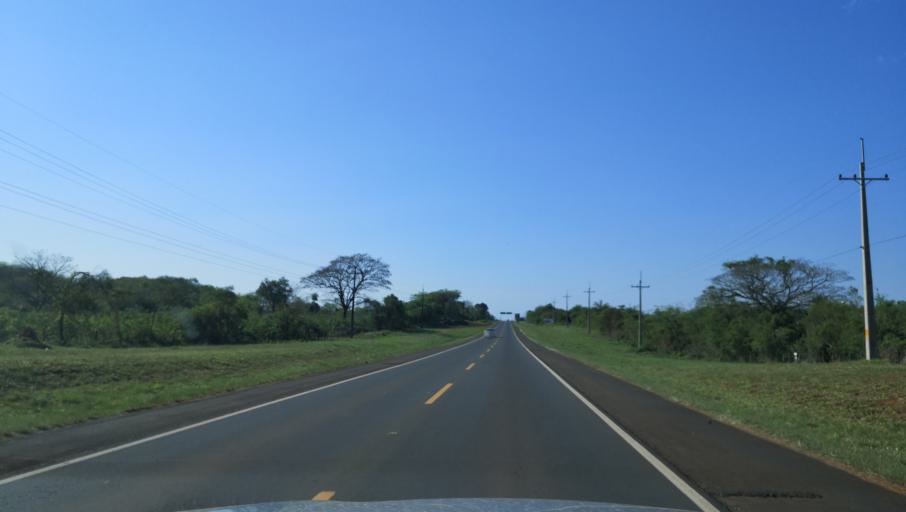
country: PY
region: Misiones
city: Santa Rosa
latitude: -26.9109
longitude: -56.8589
